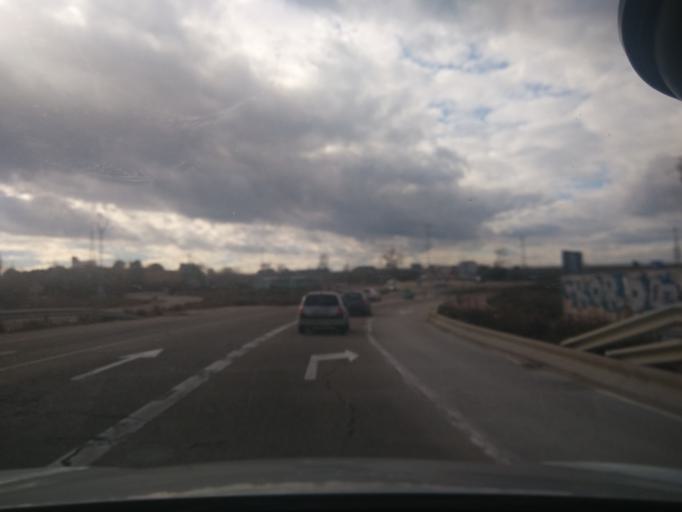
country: ES
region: Madrid
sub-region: Provincia de Madrid
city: Las Tablas
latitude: 40.5486
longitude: -3.7015
